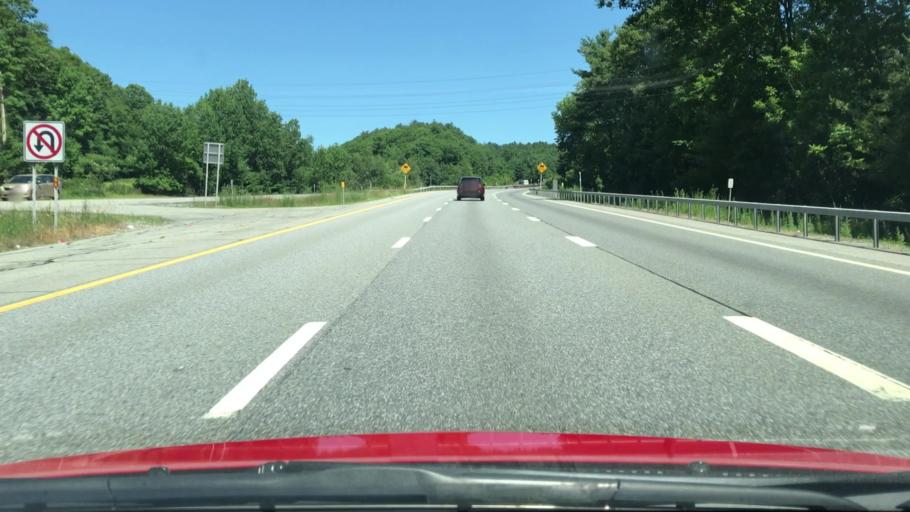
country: US
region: New York
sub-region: Warren County
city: Warrensburg
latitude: 43.4507
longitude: -73.7341
